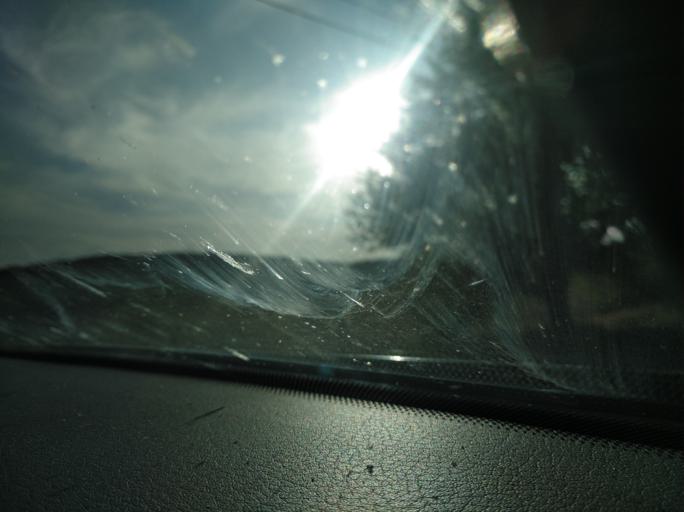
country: PT
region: Evora
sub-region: Estremoz
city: Estremoz
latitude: 38.9495
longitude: -7.4946
